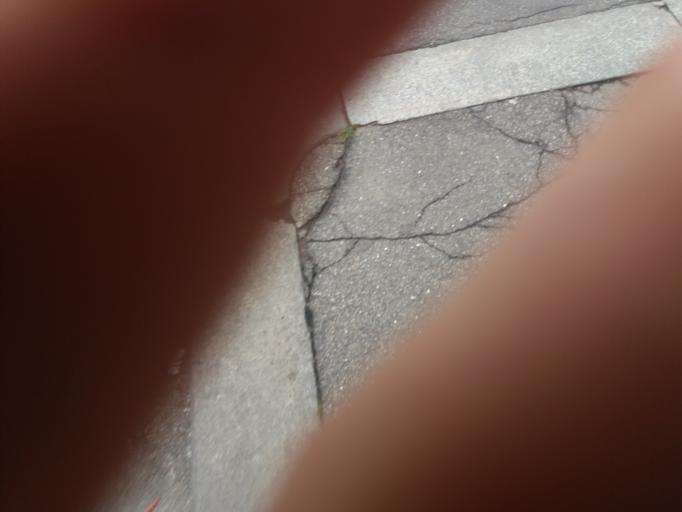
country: IT
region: Piedmont
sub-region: Provincia di Torino
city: Lesna
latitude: 45.0740
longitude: 7.6298
